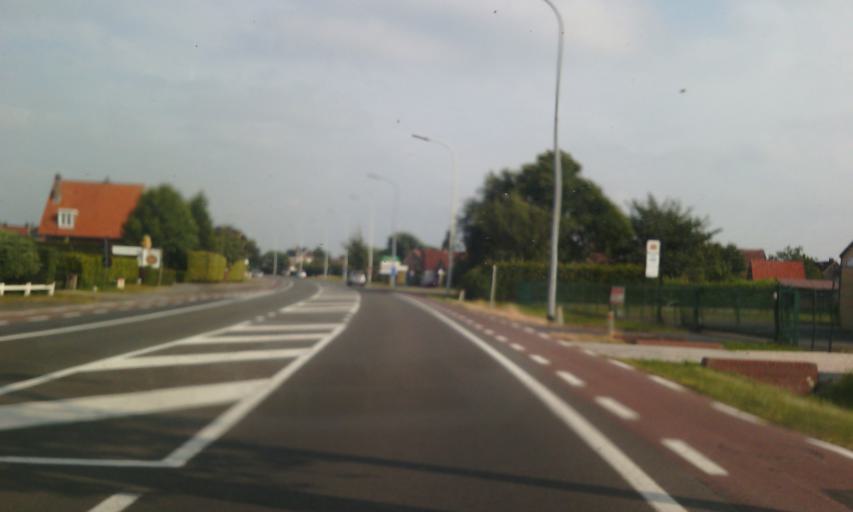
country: BE
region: Flanders
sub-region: Provincie Oost-Vlaanderen
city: Lovendegem
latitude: 51.1098
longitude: 3.6138
